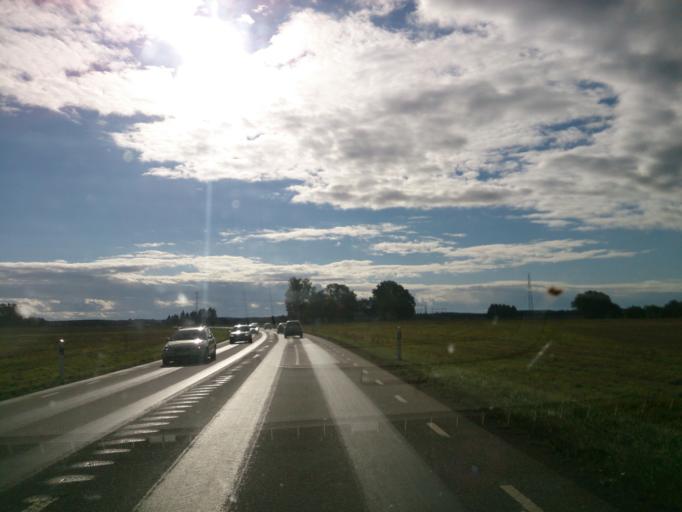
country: SE
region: Skane
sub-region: Sjobo Kommun
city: Sjoebo
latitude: 55.6289
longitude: 13.6822
